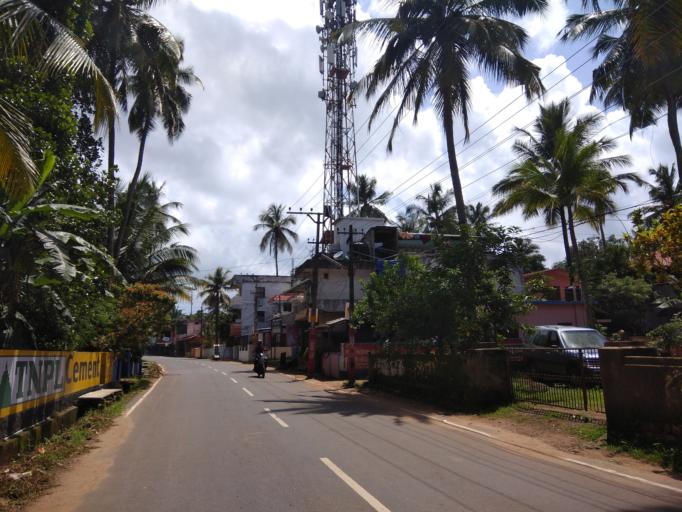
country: IN
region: Kerala
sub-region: Thrissur District
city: Avanoor
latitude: 10.5527
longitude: 76.1534
